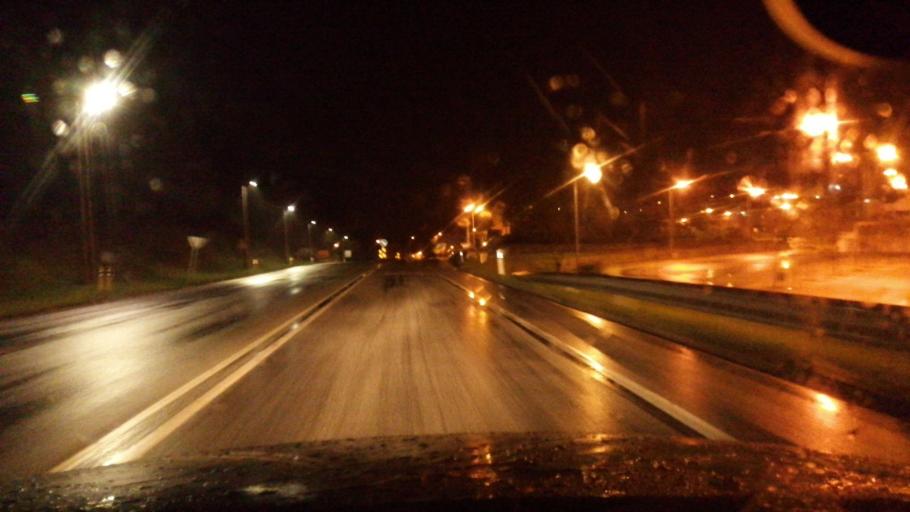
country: PT
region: Viseu
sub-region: Sernancelhe
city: Sernancelhe
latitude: 40.8962
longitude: -7.4887
